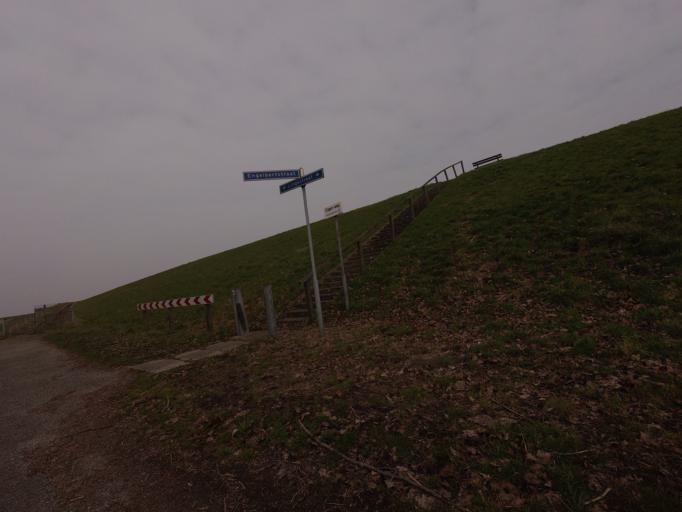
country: NL
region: North Brabant
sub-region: Gemeente Woensdrecht
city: Woensdrecht
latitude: 51.3485
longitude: 4.2285
